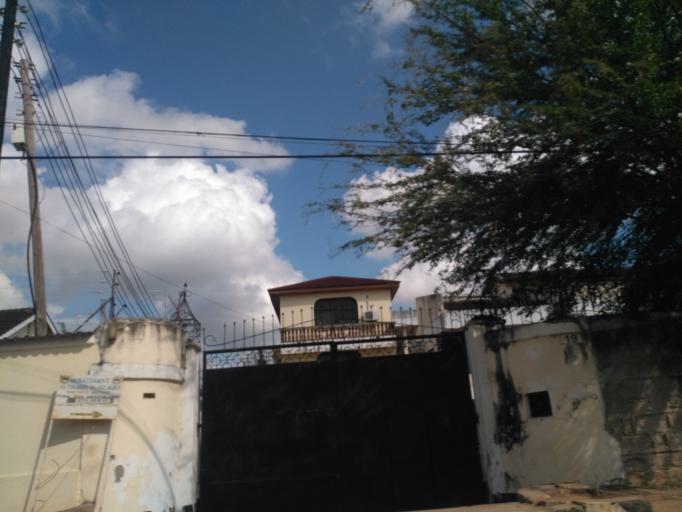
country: TZ
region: Dar es Salaam
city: Magomeni
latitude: -6.7573
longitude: 39.2452
